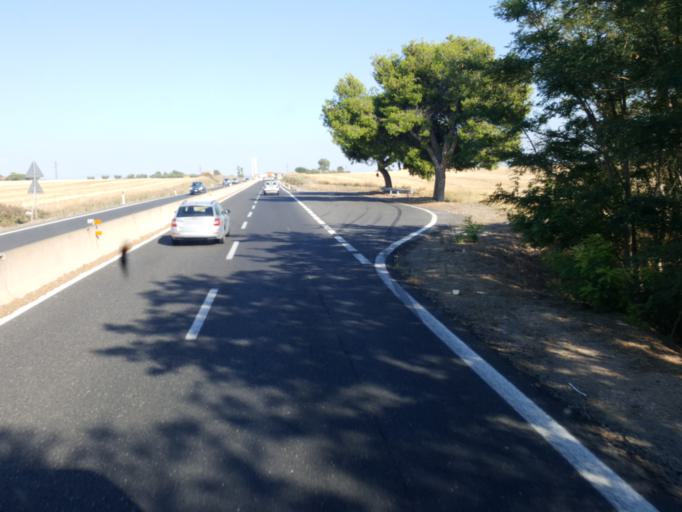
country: IT
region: Latium
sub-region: Provincia di Viterbo
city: Montalto di Castro
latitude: 42.3673
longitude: 11.5709
